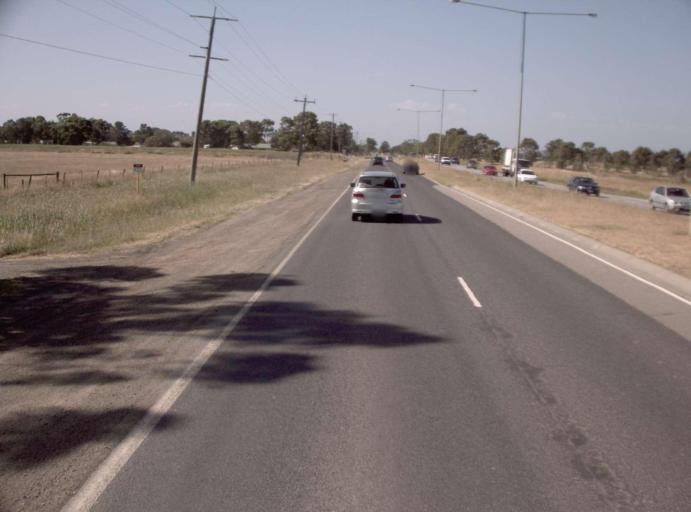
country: AU
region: Victoria
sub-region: Frankston
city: Sandhurst
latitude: -38.0473
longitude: 145.2088
